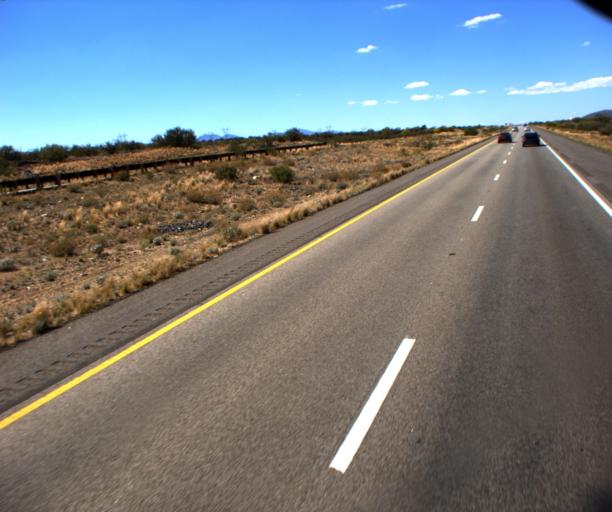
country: US
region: Arizona
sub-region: Mohave County
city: Kingman
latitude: 34.8627
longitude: -113.6418
